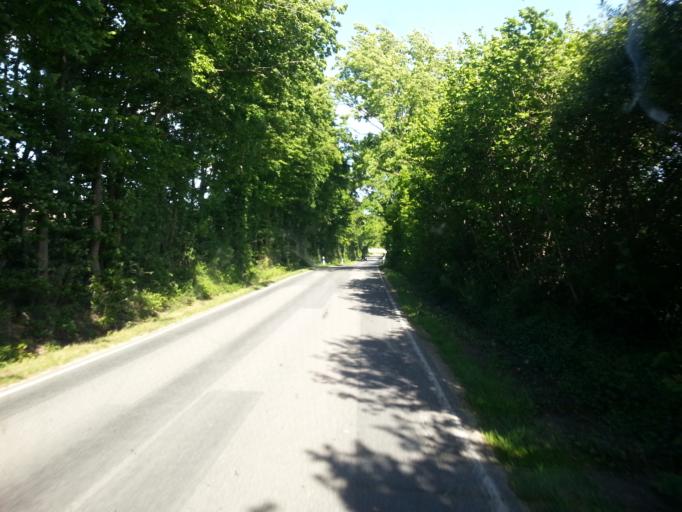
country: DE
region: Schleswig-Holstein
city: Ratekau
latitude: 53.9900
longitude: 10.7249
